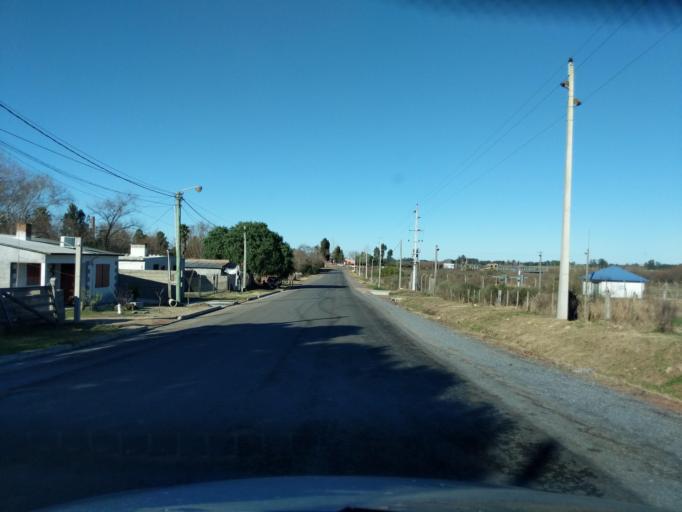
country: UY
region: Florida
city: Florida
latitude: -34.1013
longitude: -56.2419
